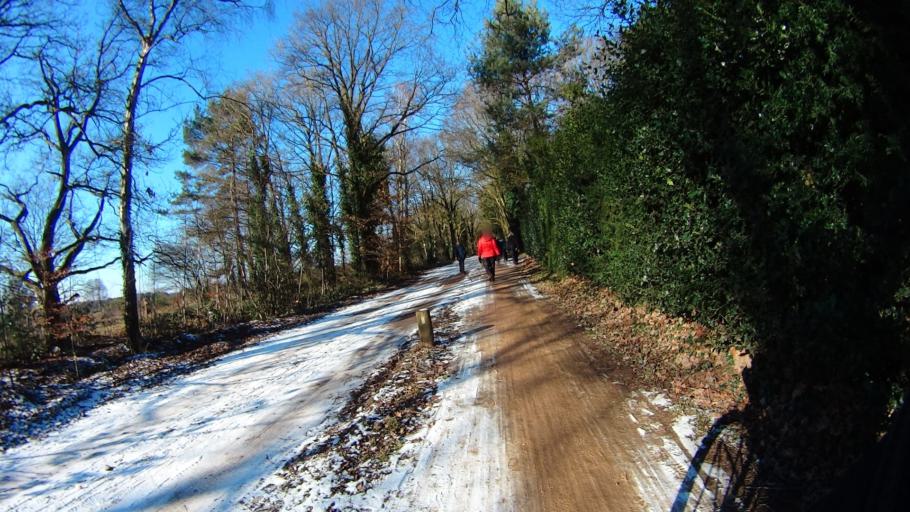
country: NL
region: North Holland
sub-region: Gemeente Laren
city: Laren
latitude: 52.2476
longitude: 5.2061
